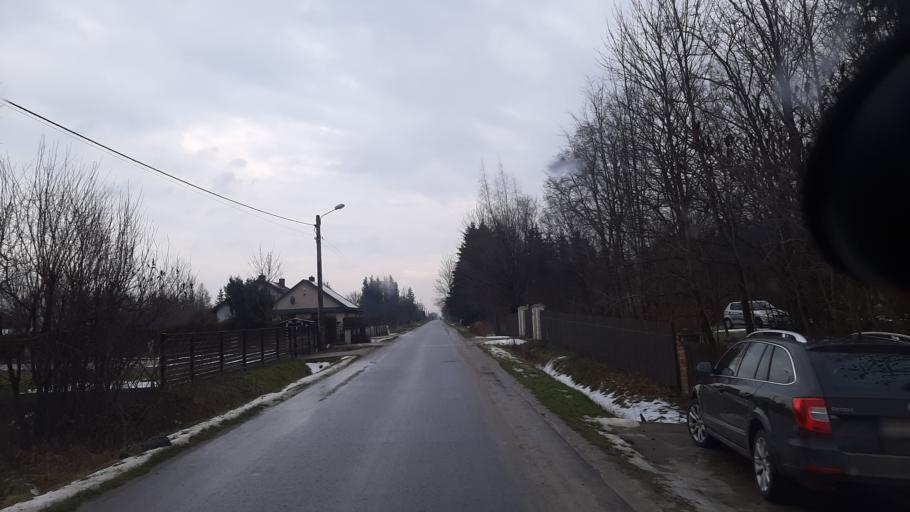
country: PL
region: Lublin Voivodeship
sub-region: Powiat lubelski
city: Jastkow
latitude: 51.3438
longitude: 22.4945
